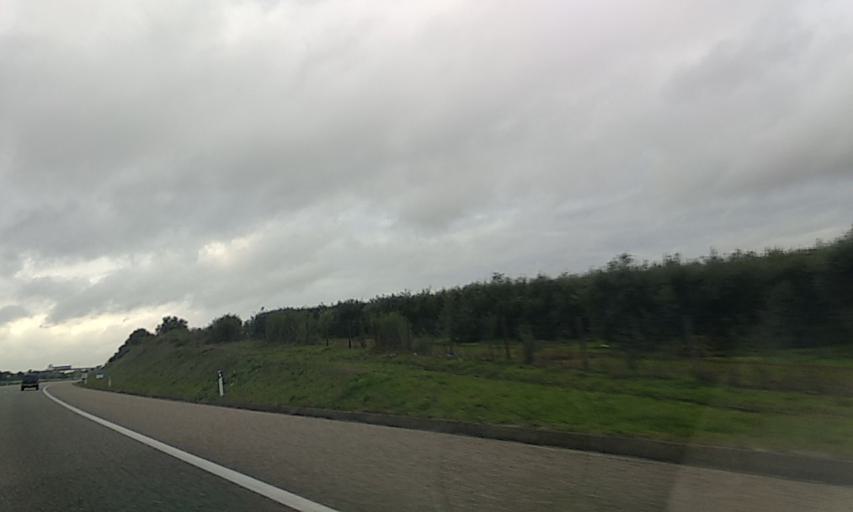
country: PT
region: Santarem
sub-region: Santarem
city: Santarem
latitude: 39.2949
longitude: -8.6877
